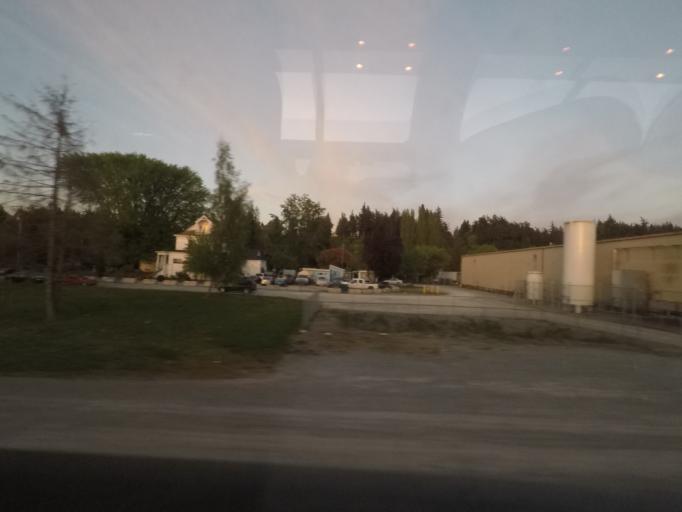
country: US
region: Washington
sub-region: Skagit County
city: Mount Vernon
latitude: 48.4134
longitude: -122.3353
